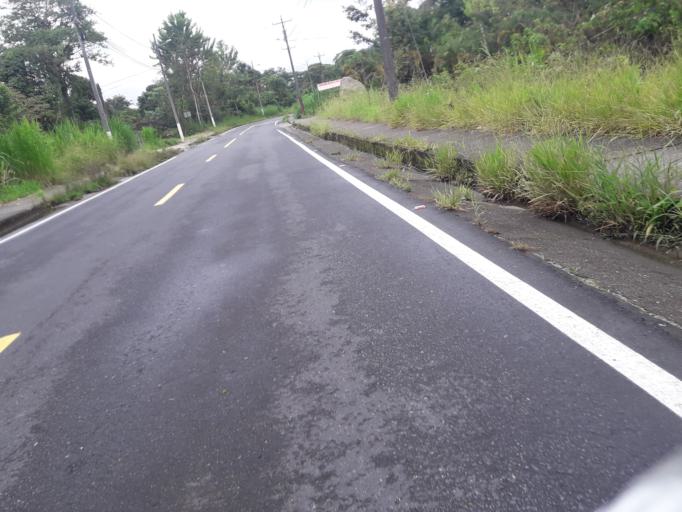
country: EC
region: Napo
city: Tena
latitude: -0.9627
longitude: -77.8574
